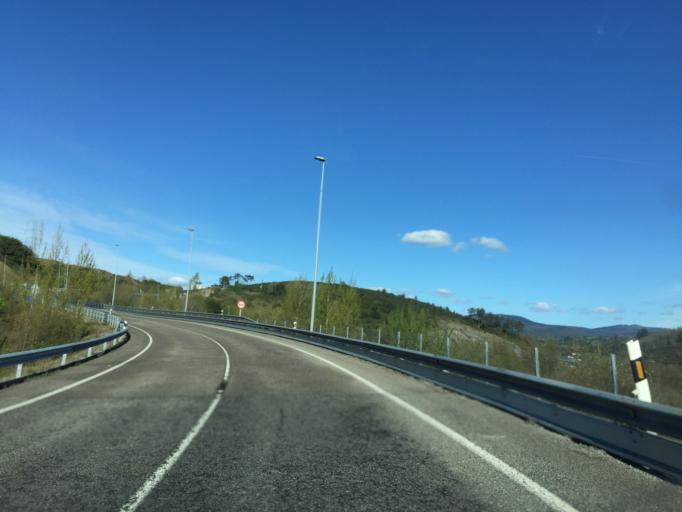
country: ES
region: Asturias
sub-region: Province of Asturias
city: Llanera
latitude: 43.3637
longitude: -5.9488
